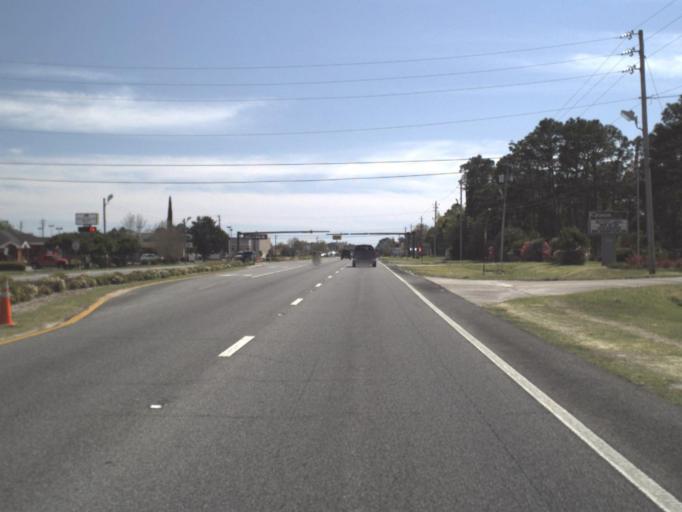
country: US
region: Florida
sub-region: Bay County
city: Hiland Park
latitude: 30.1991
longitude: -85.6498
